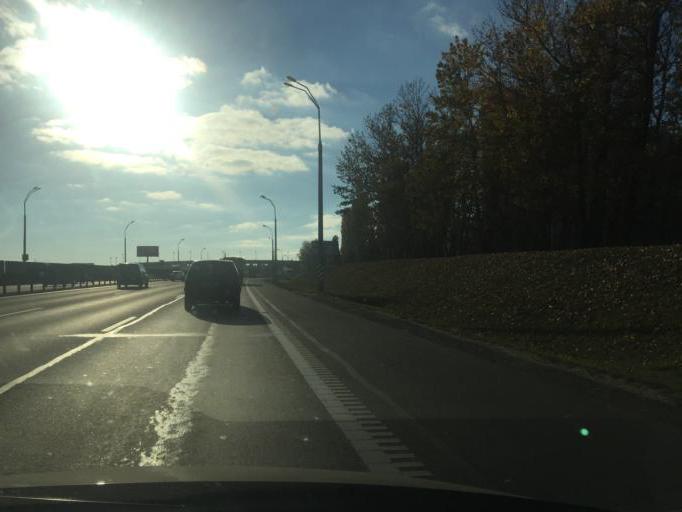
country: BY
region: Minsk
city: Vyaliki Trastsyanets
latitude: 53.8384
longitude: 27.6591
